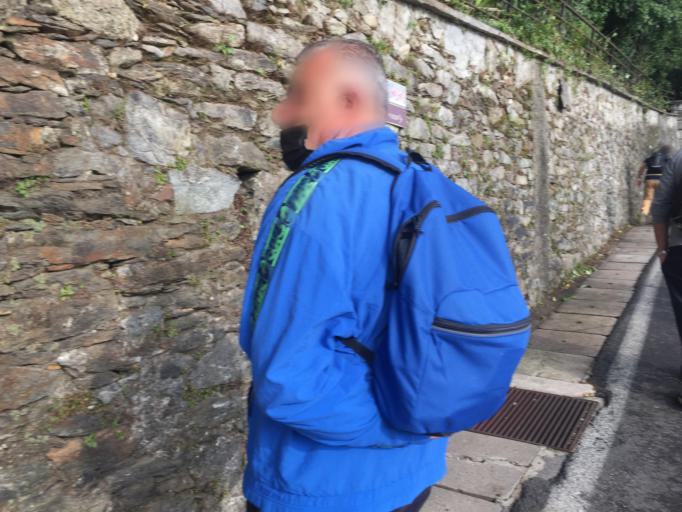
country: IT
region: Piedmont
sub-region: Provincia Verbano-Cusio-Ossola
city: Ghiffa
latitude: 45.9583
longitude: 8.6189
